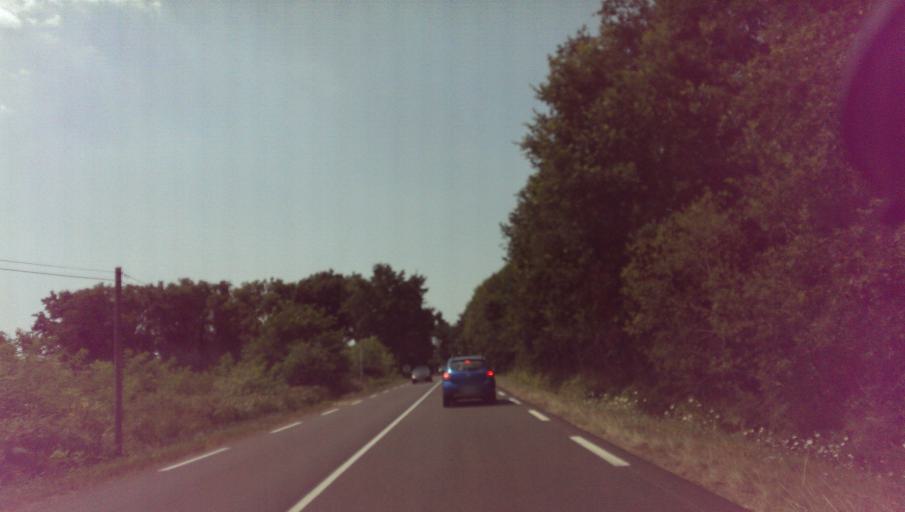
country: FR
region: Aquitaine
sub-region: Departement des Landes
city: Sabres
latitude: 44.1417
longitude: -0.7259
